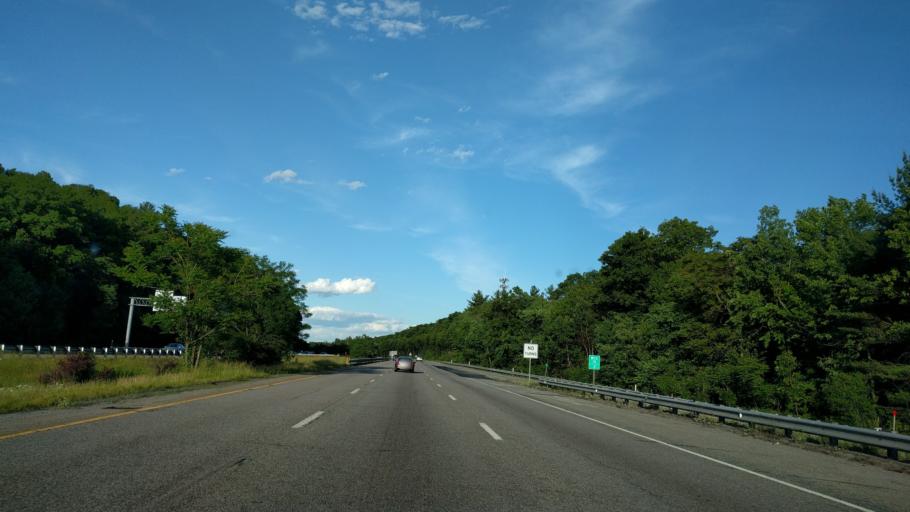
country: US
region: Massachusetts
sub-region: Worcester County
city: Northborough
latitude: 42.3323
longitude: -71.6770
